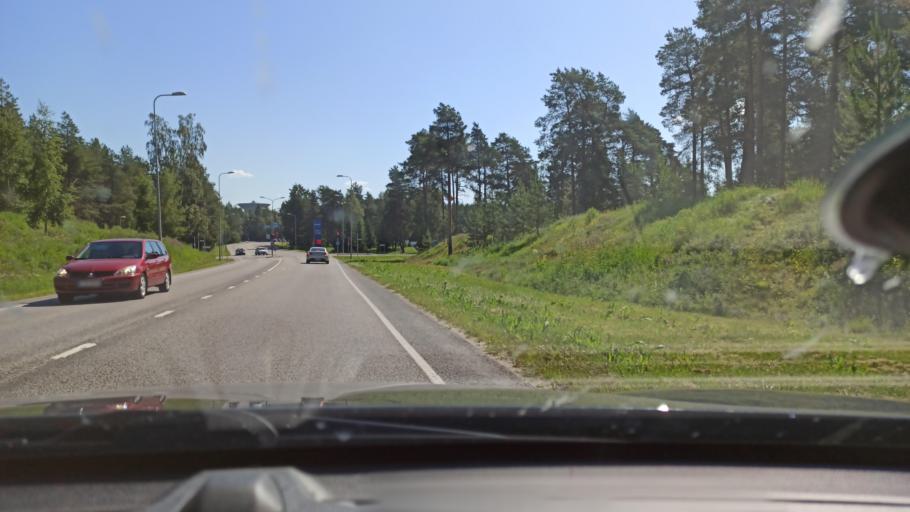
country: FI
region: Northern Ostrobothnia
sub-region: Oulu
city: Oulu
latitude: 65.0396
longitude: 25.4628
